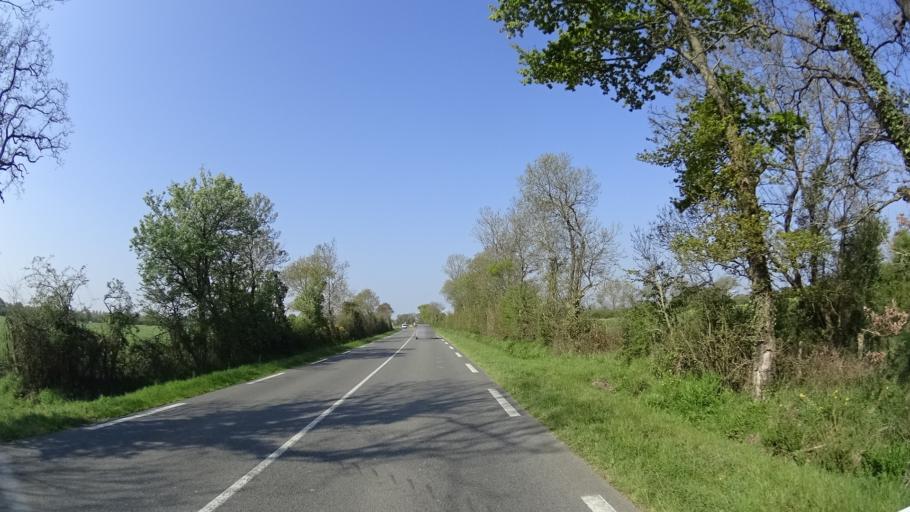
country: FR
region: Pays de la Loire
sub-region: Departement de la Loire-Atlantique
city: Saint-Hilaire-de-Chaleons
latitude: 47.0763
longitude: -1.8826
